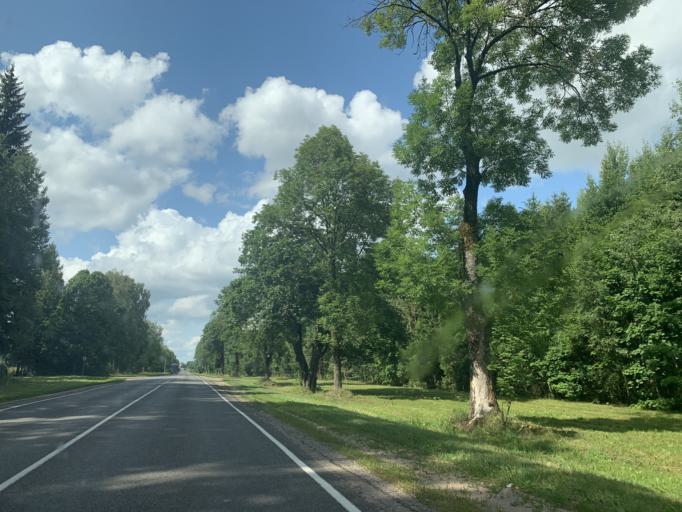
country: BY
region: Minsk
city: Enyerhyetykaw
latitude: 53.5725
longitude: 27.0619
